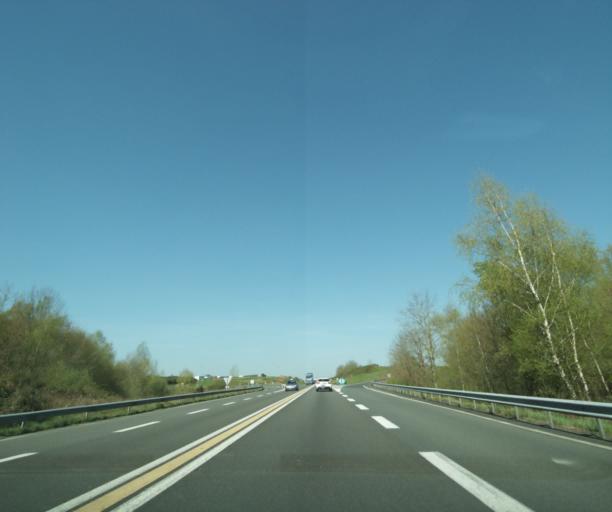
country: FR
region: Auvergne
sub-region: Departement de l'Allier
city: Diou
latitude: 46.5022
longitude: 3.7848
